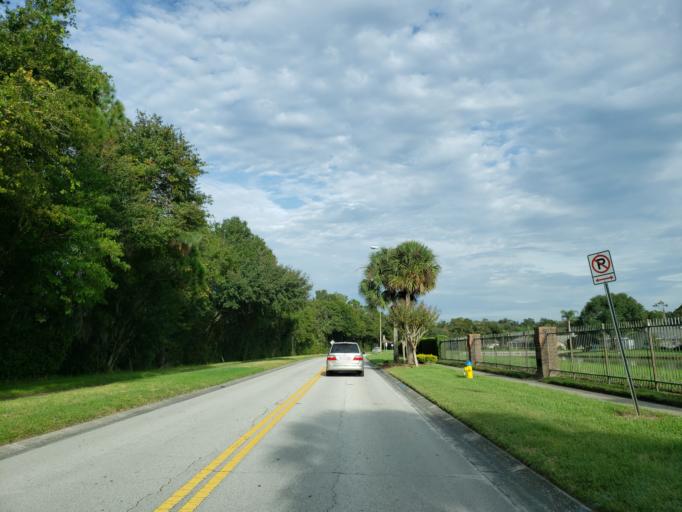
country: US
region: Florida
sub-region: Hillsborough County
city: Bloomingdale
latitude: 27.8853
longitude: -82.2516
